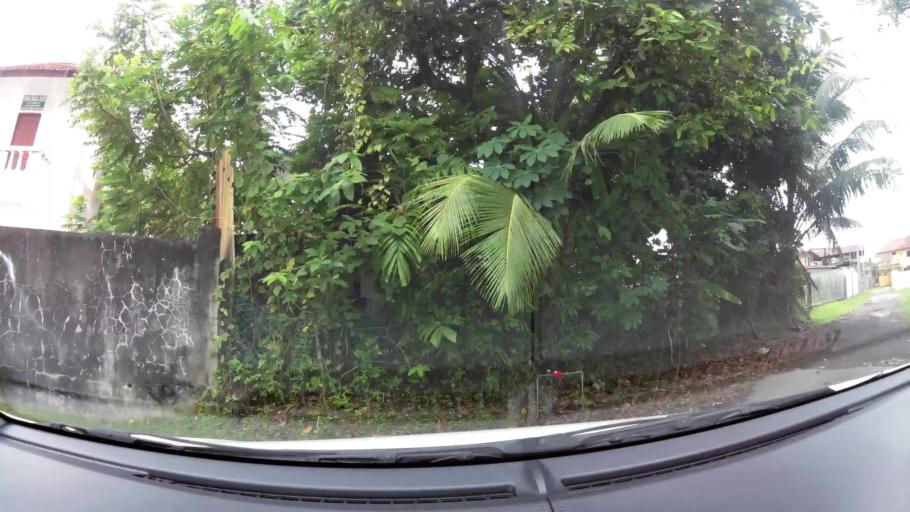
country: BN
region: Brunei and Muara
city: Bandar Seri Begawan
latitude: 4.8994
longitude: 114.9177
